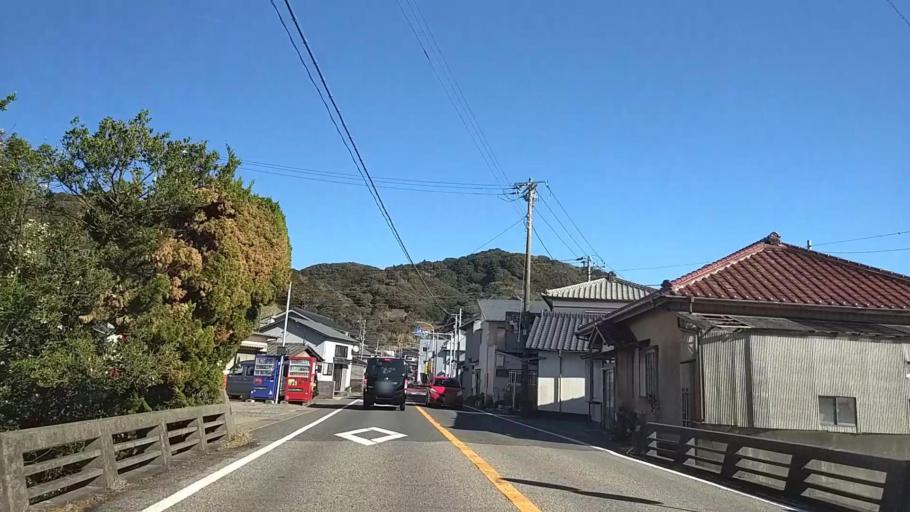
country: JP
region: Chiba
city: Kawaguchi
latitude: 35.0361
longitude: 140.0101
